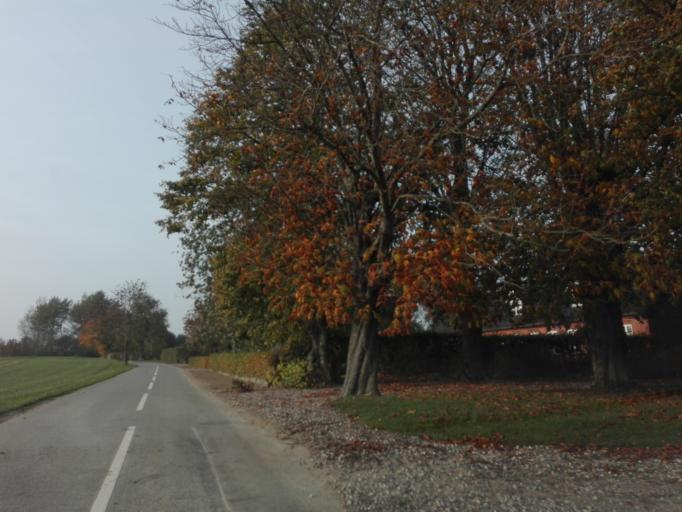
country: DK
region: Central Jutland
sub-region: Arhus Kommune
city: Solbjerg
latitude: 56.0224
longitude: 10.0992
